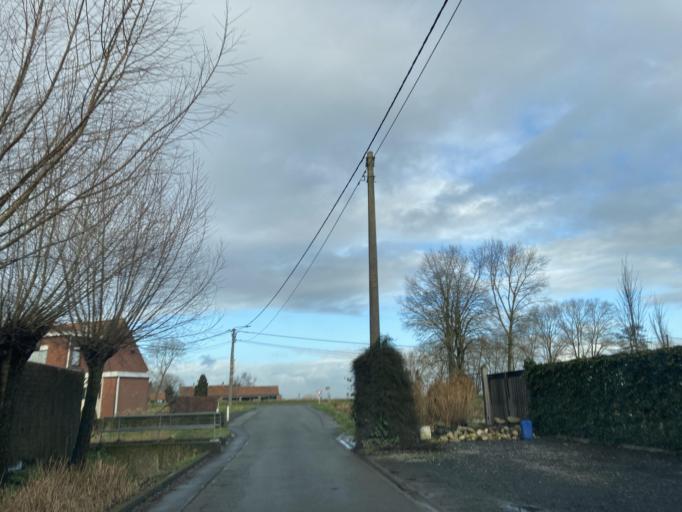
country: BE
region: Flanders
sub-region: Provincie West-Vlaanderen
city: Tielt
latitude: 51.0339
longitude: 3.3413
